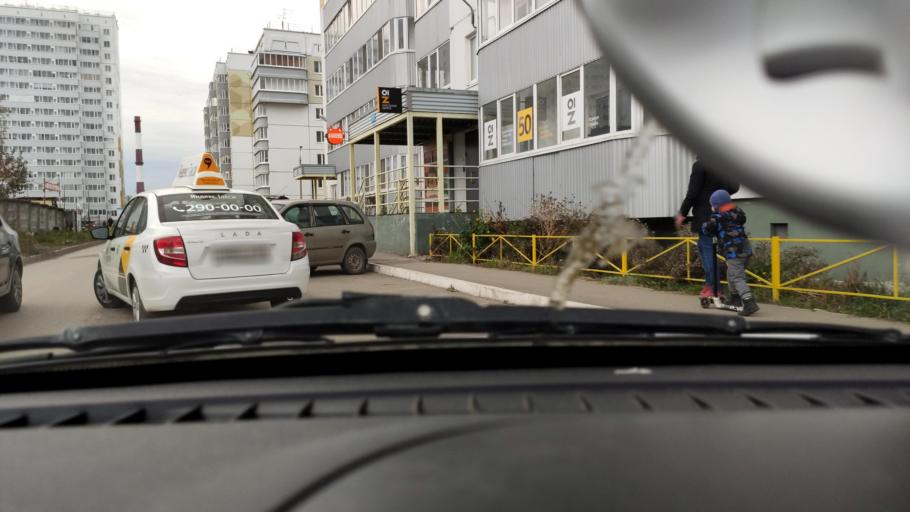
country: RU
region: Perm
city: Kondratovo
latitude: 57.9873
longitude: 56.1183
